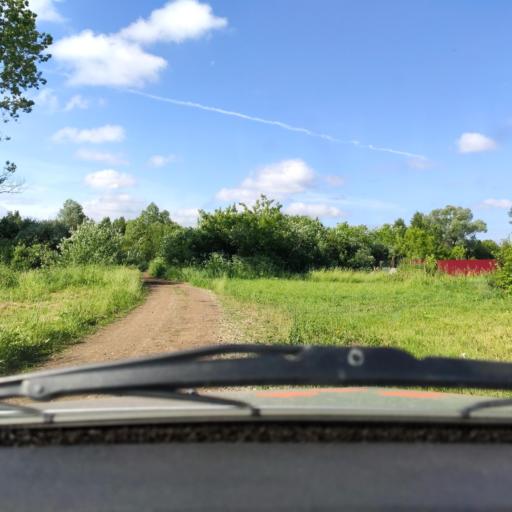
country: RU
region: Bashkortostan
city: Iglino
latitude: 54.7974
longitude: 56.2971
